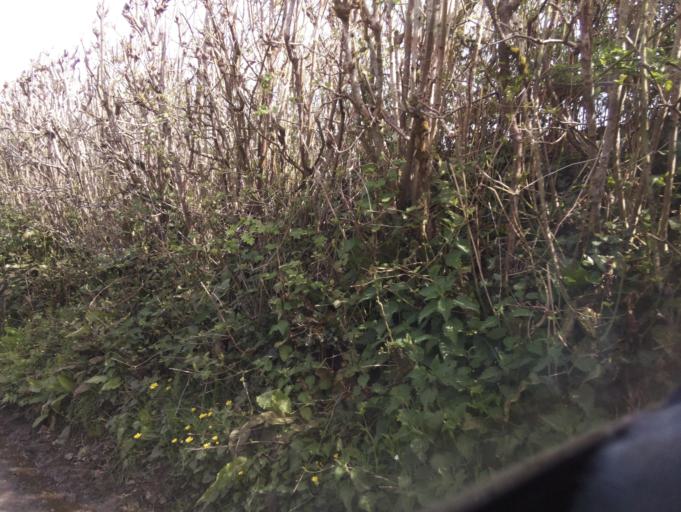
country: GB
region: England
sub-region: Dorset
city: Sherborne
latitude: 50.9758
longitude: -2.5325
